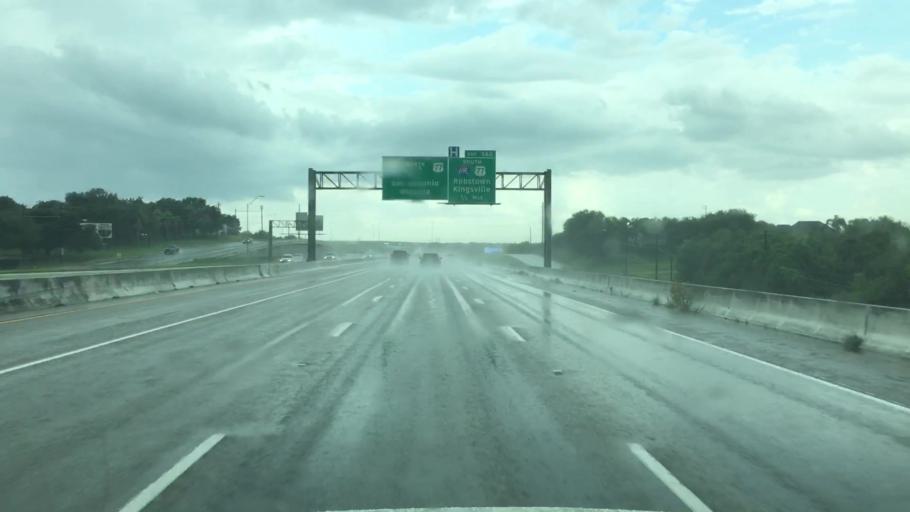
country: US
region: Texas
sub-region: Nueces County
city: Robstown
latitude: 27.8591
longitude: -97.6078
